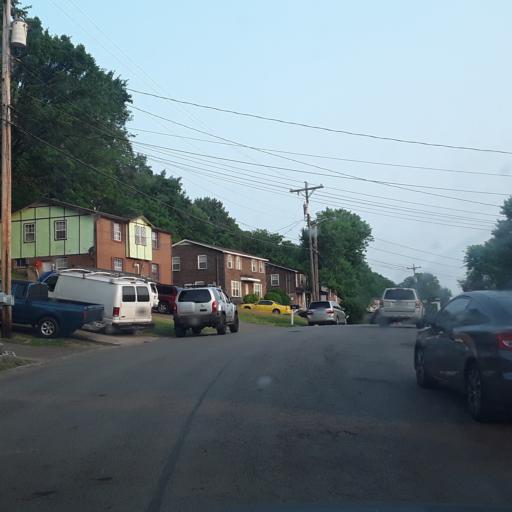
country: US
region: Tennessee
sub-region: Williamson County
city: Brentwood Estates
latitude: 36.0501
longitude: -86.7250
